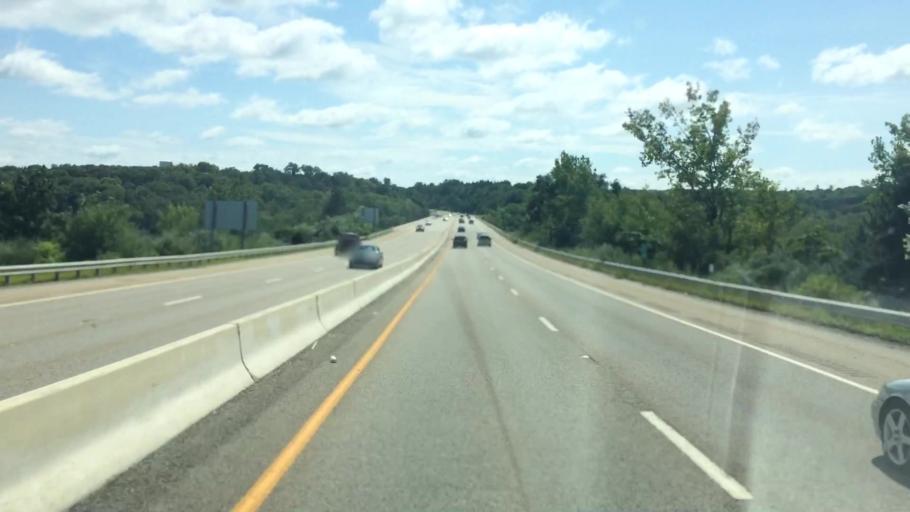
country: US
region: Rhode Island
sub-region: Providence County
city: Cumberland Hill
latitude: 41.9814
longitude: -71.4839
